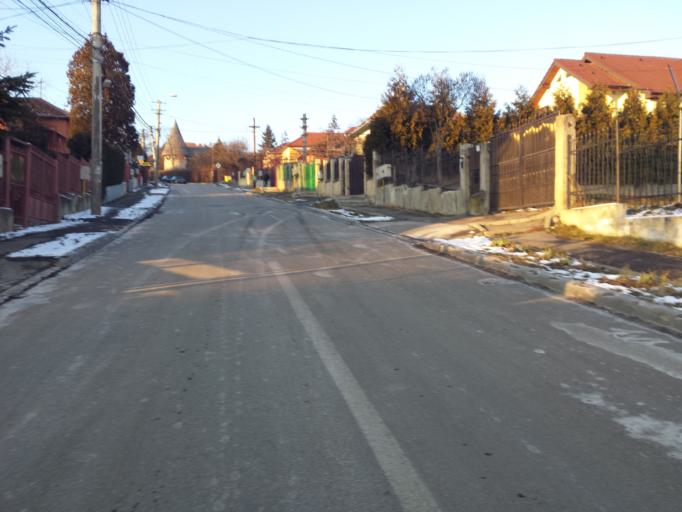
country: RO
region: Cluj
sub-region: Municipiul Cluj-Napoca
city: Cluj-Napoca
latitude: 46.7912
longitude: 23.5865
